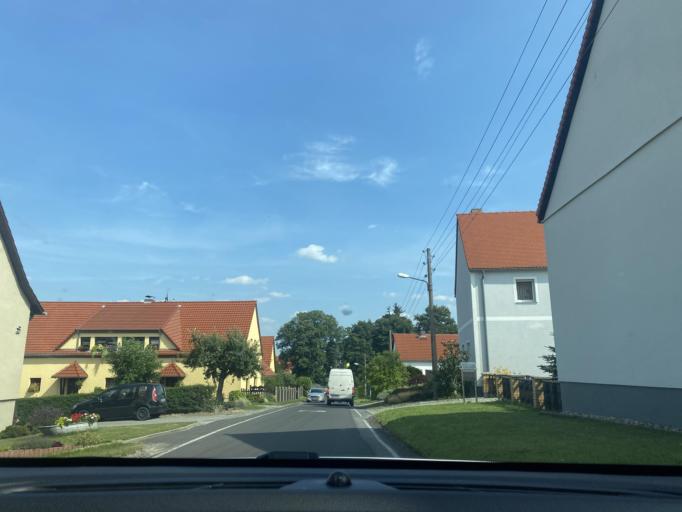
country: DE
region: Saxony
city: Goerlitz
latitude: 51.1821
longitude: 14.9763
